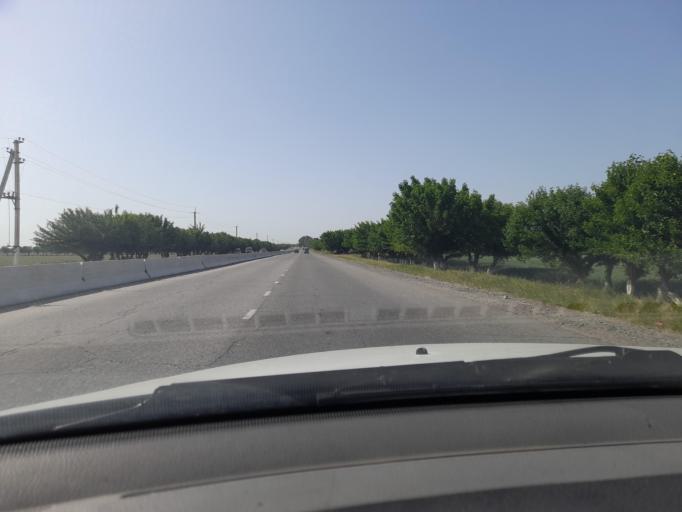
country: UZ
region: Samarqand
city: Chelak
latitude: 39.8265
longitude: 66.8389
